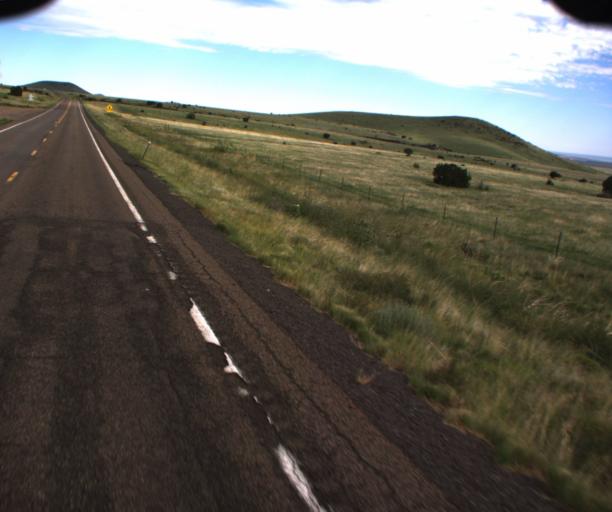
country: US
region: Arizona
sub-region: Apache County
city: Springerville
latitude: 34.2285
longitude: -109.4916
